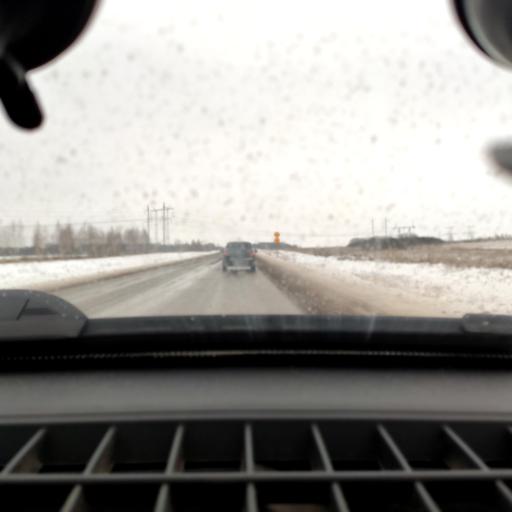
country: RU
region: Bashkortostan
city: Iglino
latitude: 54.7839
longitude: 56.4178
